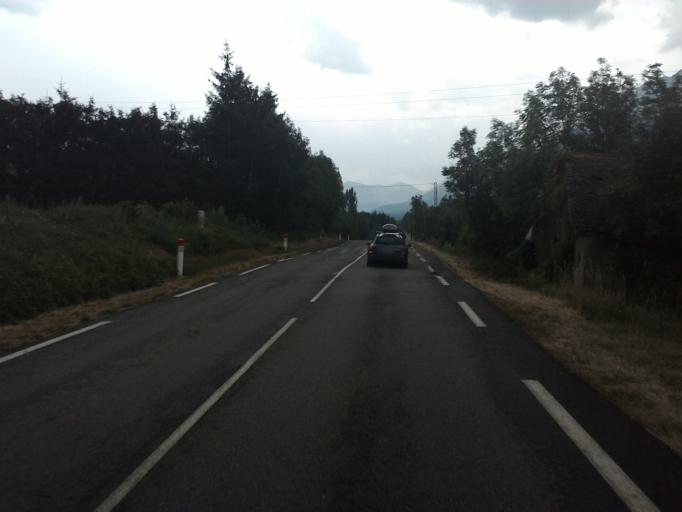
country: FR
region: Provence-Alpes-Cote d'Azur
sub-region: Departement des Hautes-Alpes
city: Saint-Bonnet-en-Champsaur
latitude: 44.7862
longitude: 5.9828
